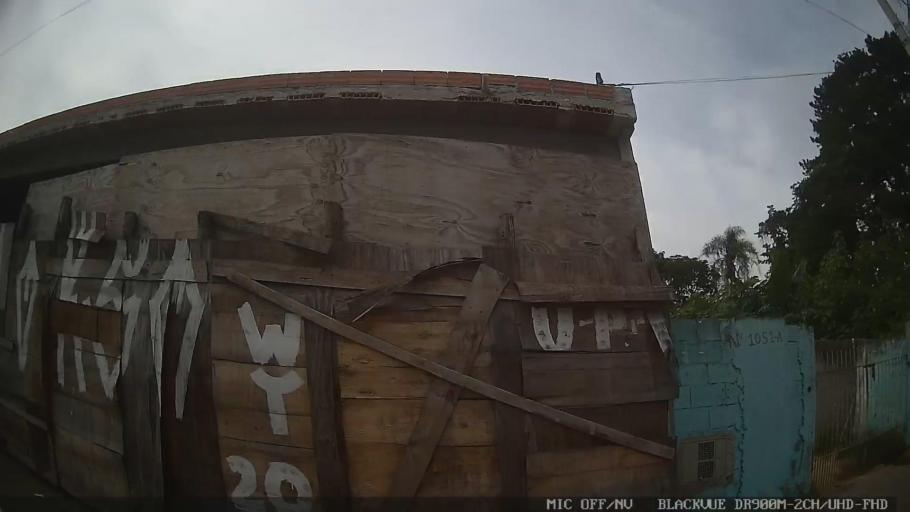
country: BR
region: Sao Paulo
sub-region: Poa
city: Poa
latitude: -23.5181
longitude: -46.3480
